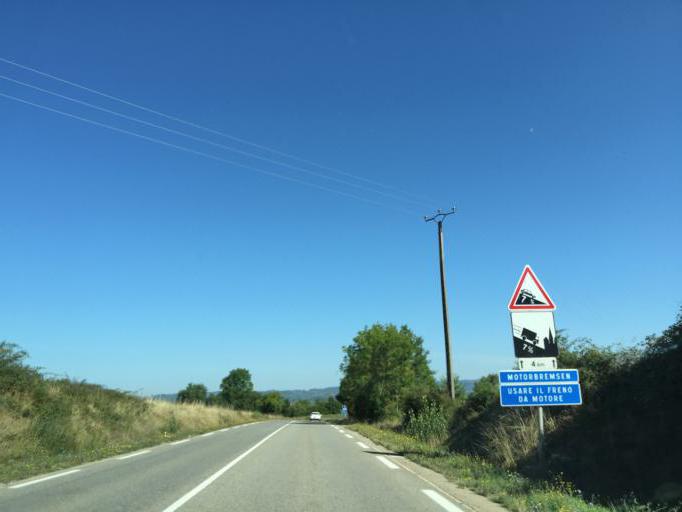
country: FR
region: Midi-Pyrenees
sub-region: Departement de l'Aveyron
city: Espalion
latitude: 44.5092
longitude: 2.7354
